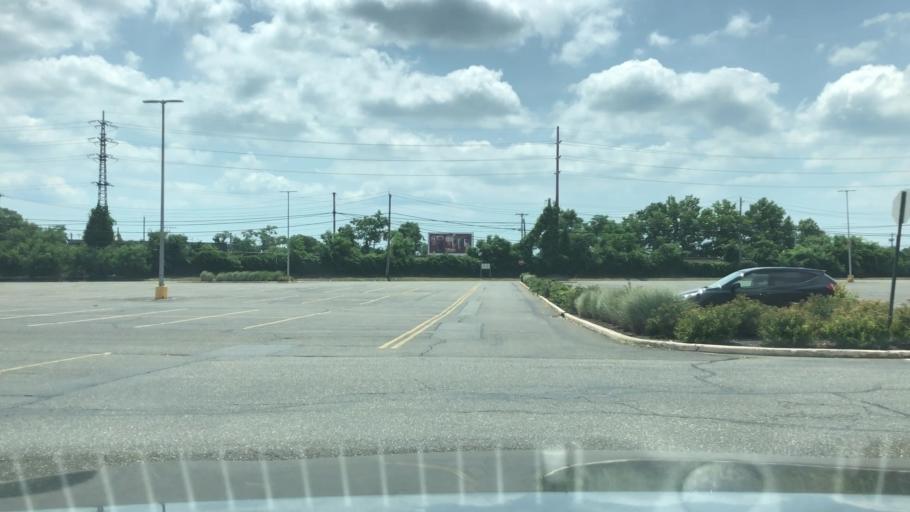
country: US
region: New York
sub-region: Nassau County
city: East Massapequa
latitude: 40.6804
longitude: -73.4344
